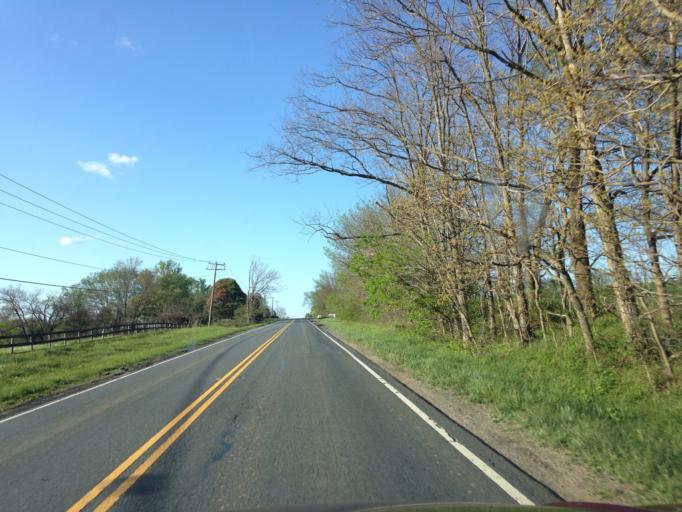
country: US
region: Virginia
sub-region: Loudoun County
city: Lovettsville
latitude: 39.2254
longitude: -77.6572
